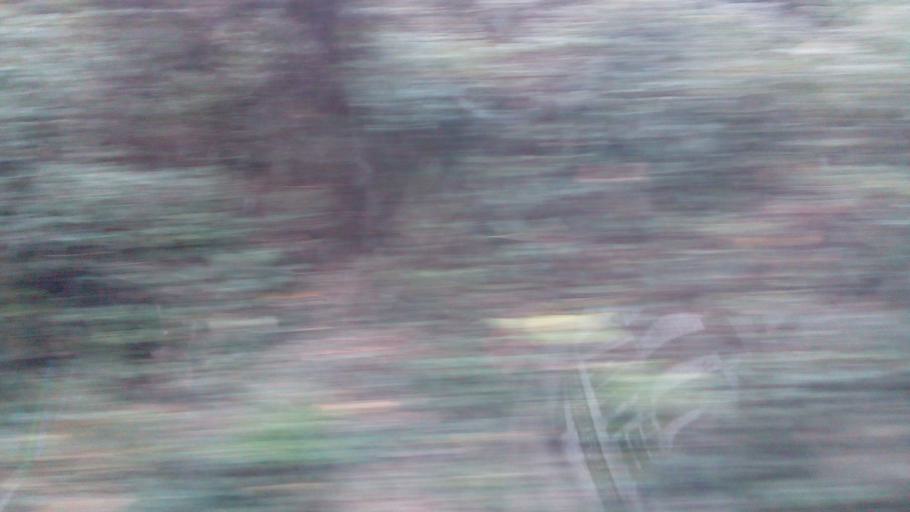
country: TW
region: Taiwan
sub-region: Hualien
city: Hualian
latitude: 24.3459
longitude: 121.3159
